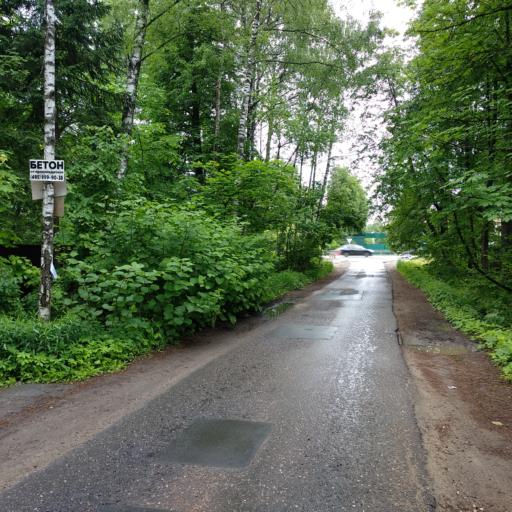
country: RU
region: Moskovskaya
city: Nekrasovskiy
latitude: 56.1201
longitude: 37.5209
